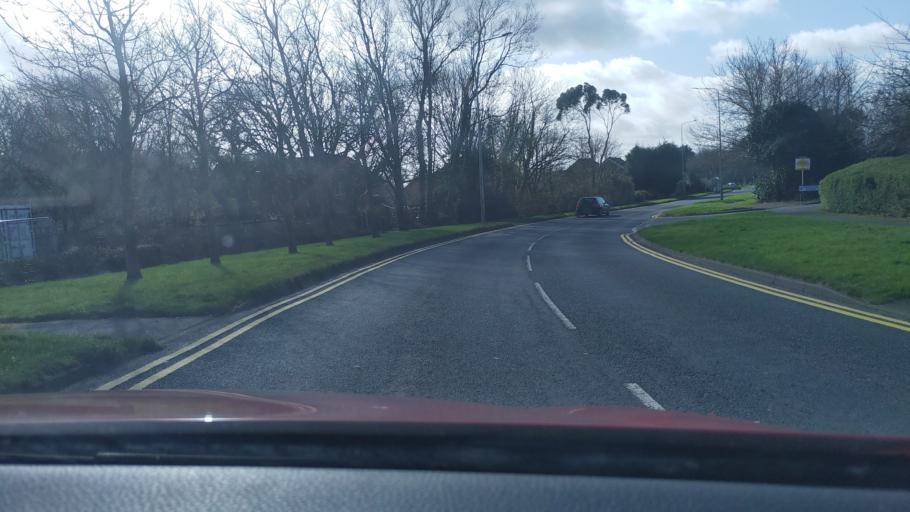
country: GB
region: England
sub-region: Lancashire
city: Preston
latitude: 53.7917
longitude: -2.6959
